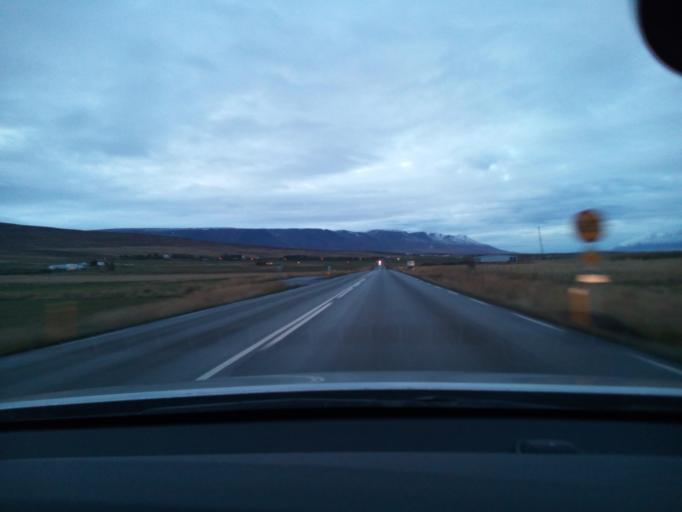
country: IS
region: Northeast
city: Akureyri
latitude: 65.7095
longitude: -18.1612
